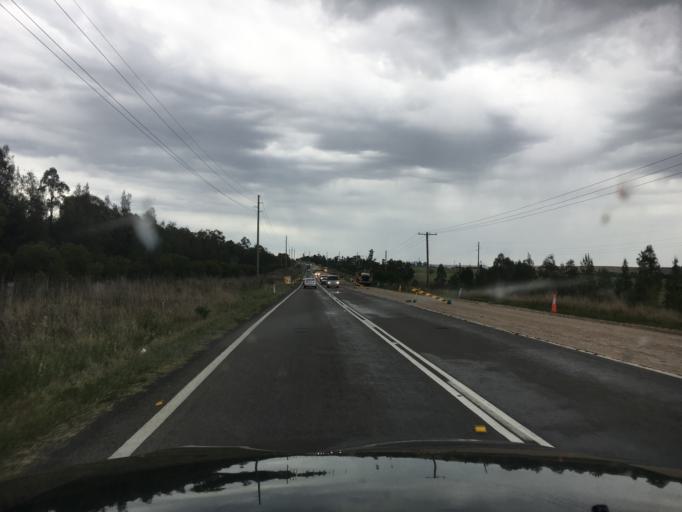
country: AU
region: New South Wales
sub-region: Muswellbrook
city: Muswellbrook
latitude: -32.1960
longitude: 150.8925
